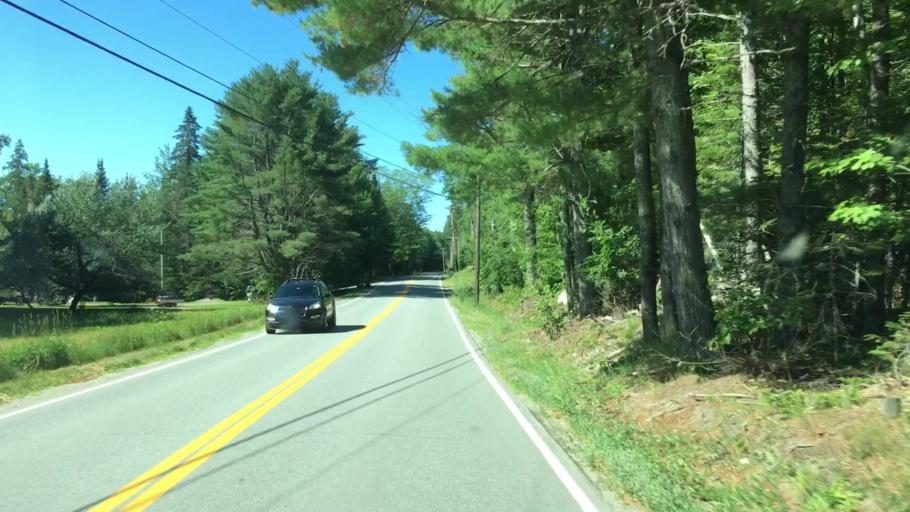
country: US
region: Maine
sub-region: Hancock County
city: Dedham
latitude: 44.7199
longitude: -68.6409
